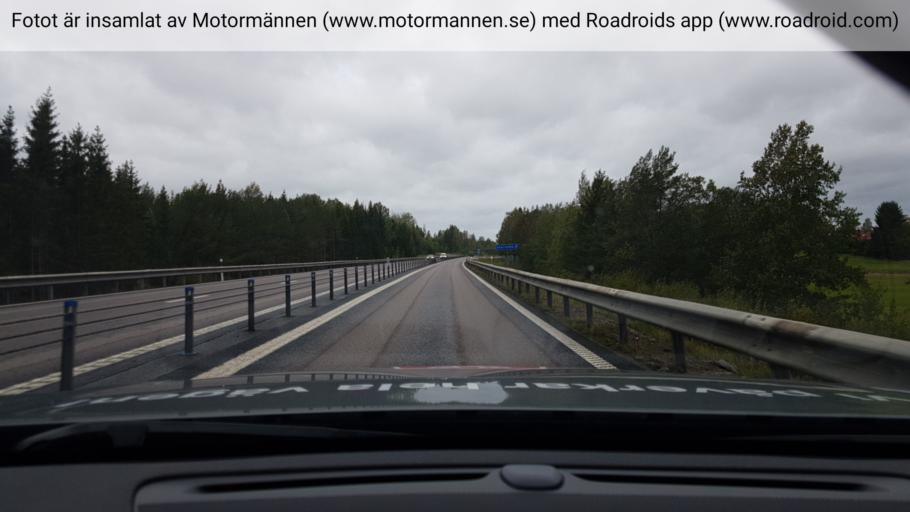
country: SE
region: Vaermland
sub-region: Karlstads Kommun
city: Skattkarr
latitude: 59.4181
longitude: 13.7224
